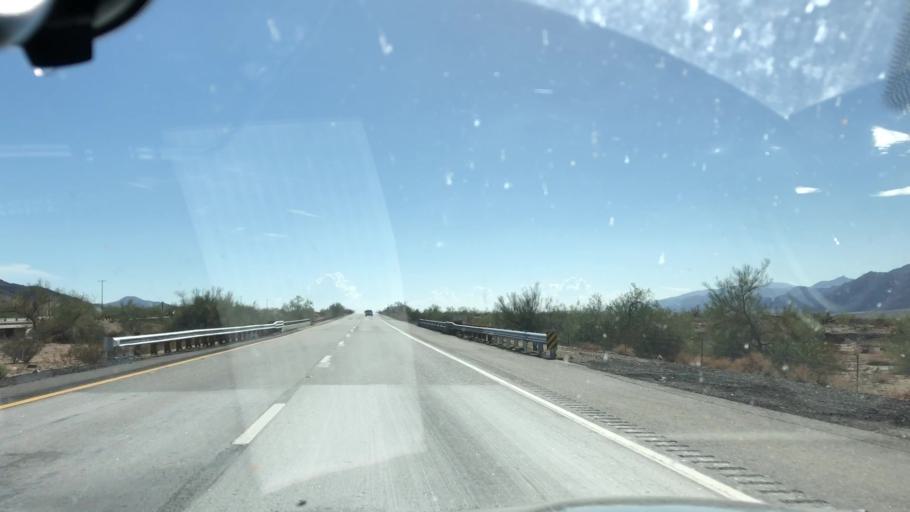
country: US
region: California
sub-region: Imperial County
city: Niland
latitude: 33.6997
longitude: -115.4663
